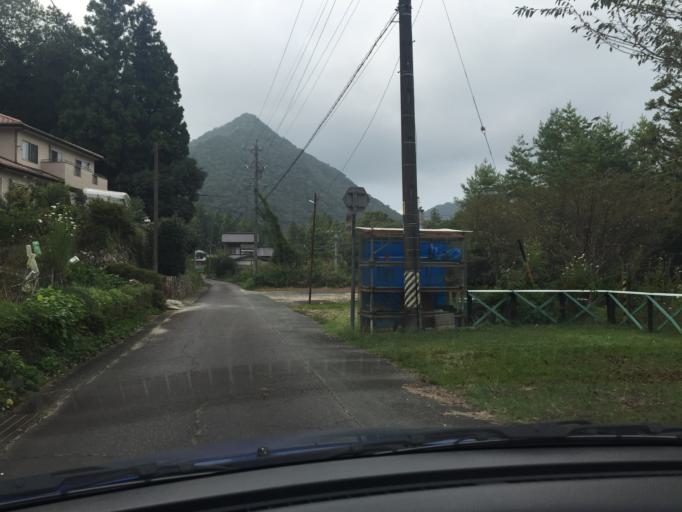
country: JP
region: Aichi
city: Shinshiro
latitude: 34.9760
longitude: 137.6139
